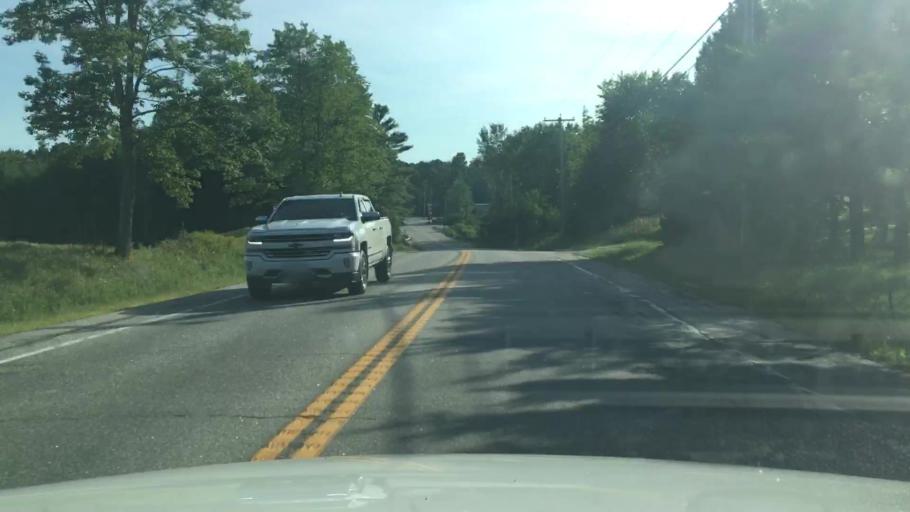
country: US
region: Maine
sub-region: Cumberland County
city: New Gloucester
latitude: 43.9196
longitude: -70.3157
